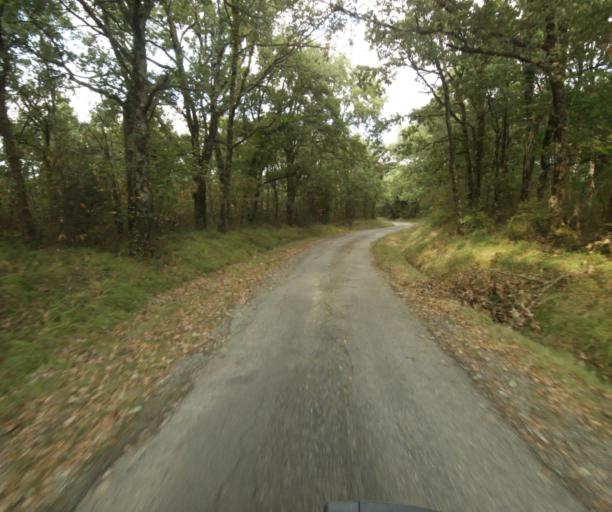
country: FR
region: Midi-Pyrenees
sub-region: Departement de la Haute-Garonne
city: Launac
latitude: 43.8289
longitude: 1.1137
